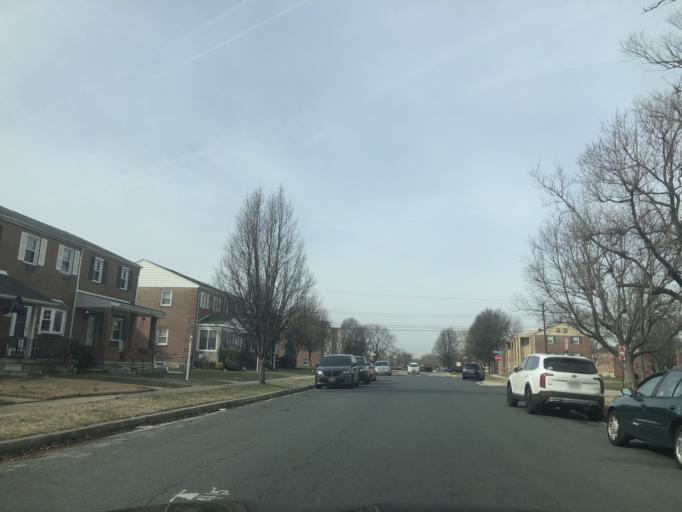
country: US
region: Maryland
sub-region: Baltimore County
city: Dundalk
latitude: 39.2672
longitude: -76.4822
